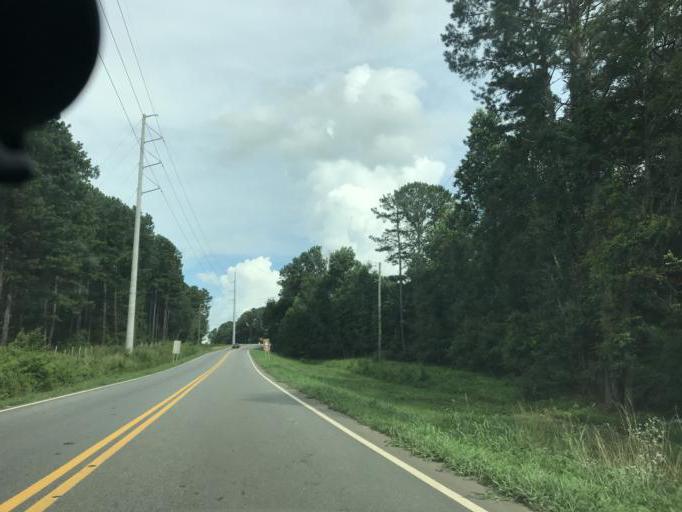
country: US
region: Georgia
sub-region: Forsyth County
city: Cumming
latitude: 34.3074
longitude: -84.2176
